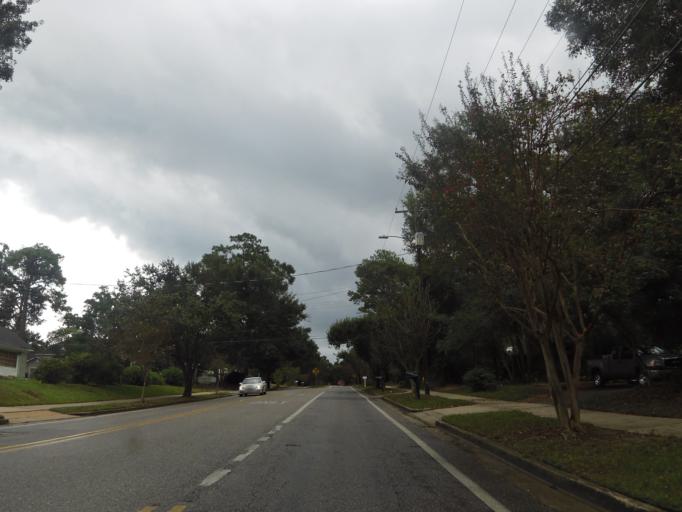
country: US
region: Alabama
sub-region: Baldwin County
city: Fairhope
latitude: 30.5230
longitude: -87.8931
